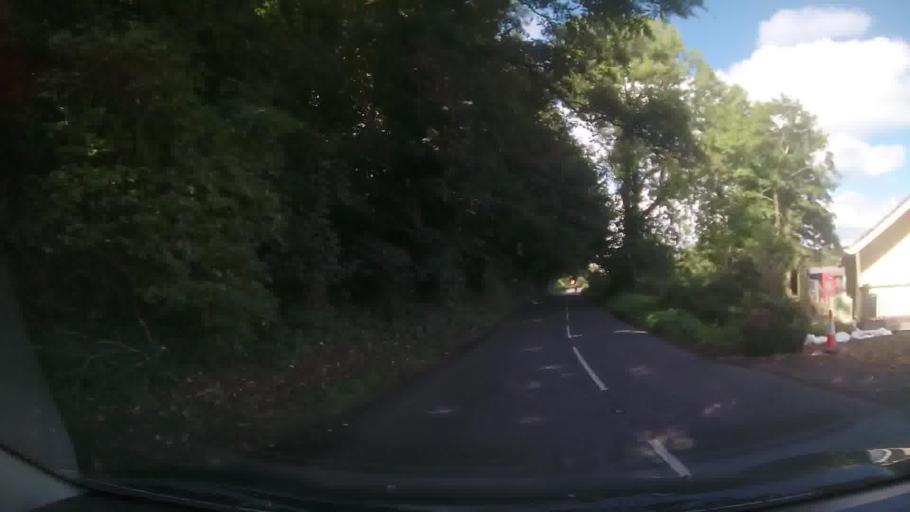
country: GB
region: Wales
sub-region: Pembrokeshire
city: Penally
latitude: 51.6565
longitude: -4.7410
